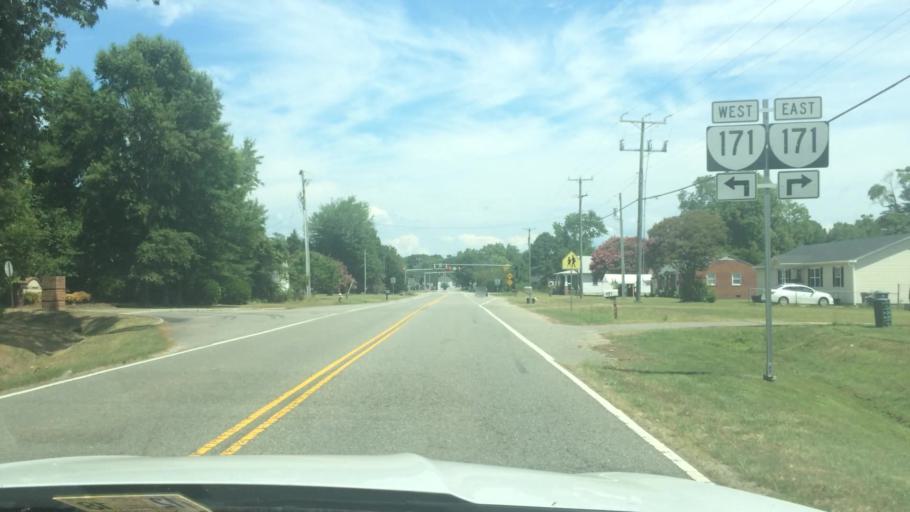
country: US
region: Virginia
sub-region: City of Poquoson
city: Poquoson
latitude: 37.1204
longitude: -76.4321
